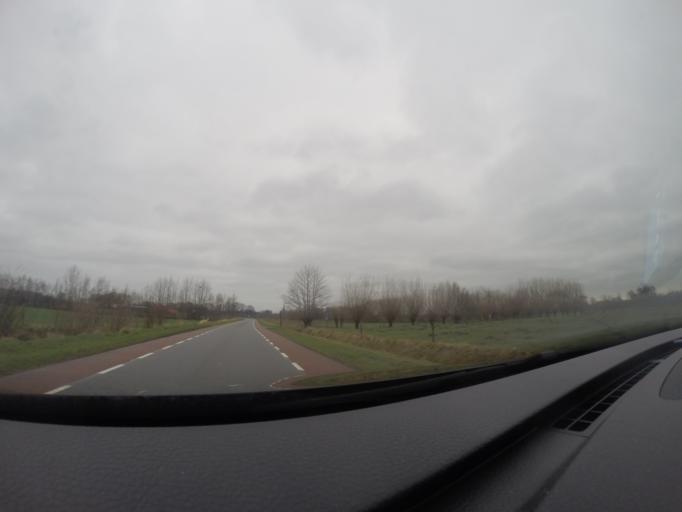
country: NL
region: Overijssel
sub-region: Gemeente Hof van Twente
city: Diepenheim
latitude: 52.1725
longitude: 6.5269
